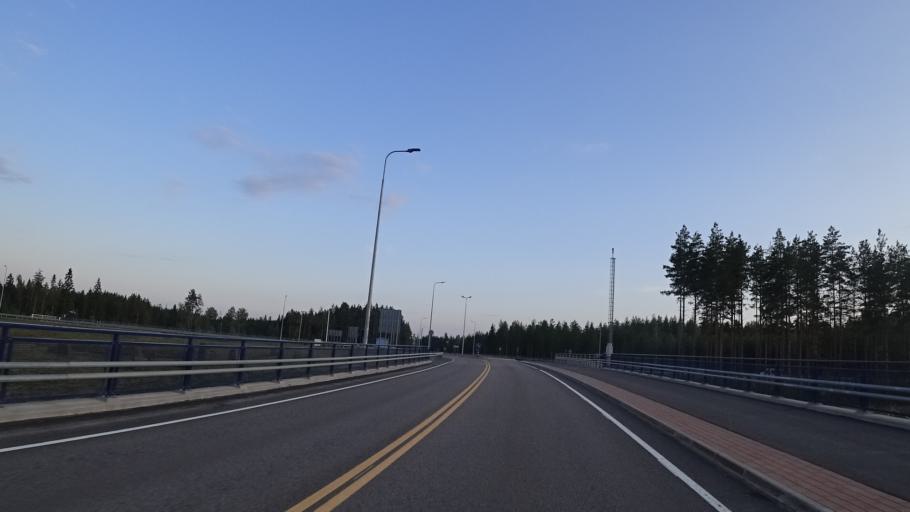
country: FI
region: Kymenlaakso
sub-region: Kotka-Hamina
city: Virojoki
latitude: 60.6054
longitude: 27.7041
